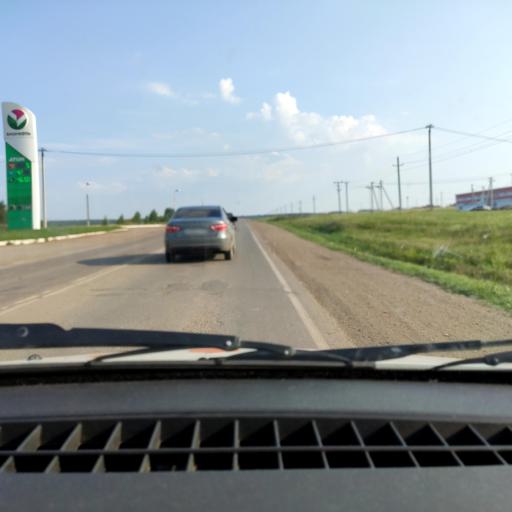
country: RU
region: Bashkortostan
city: Iglino
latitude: 54.8019
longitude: 56.4132
